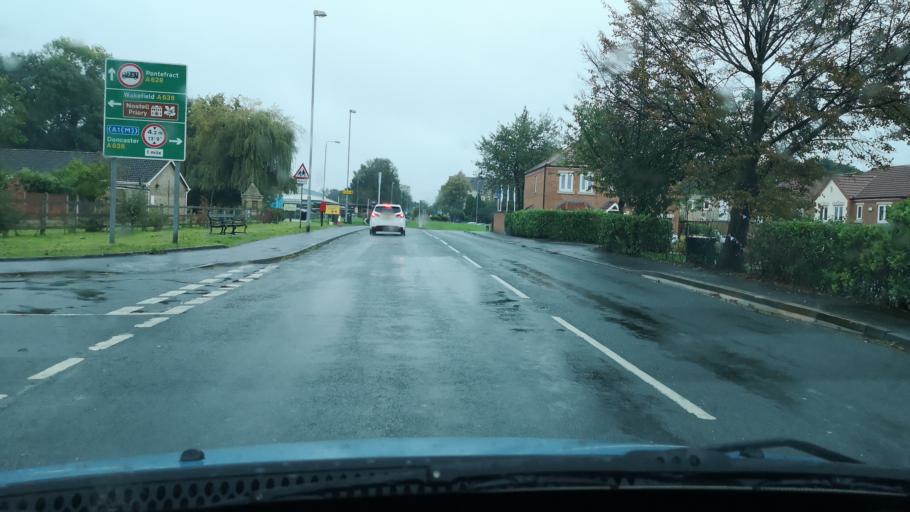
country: GB
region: England
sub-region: City and Borough of Wakefield
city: Low Ackworth
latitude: 53.6398
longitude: -1.3358
